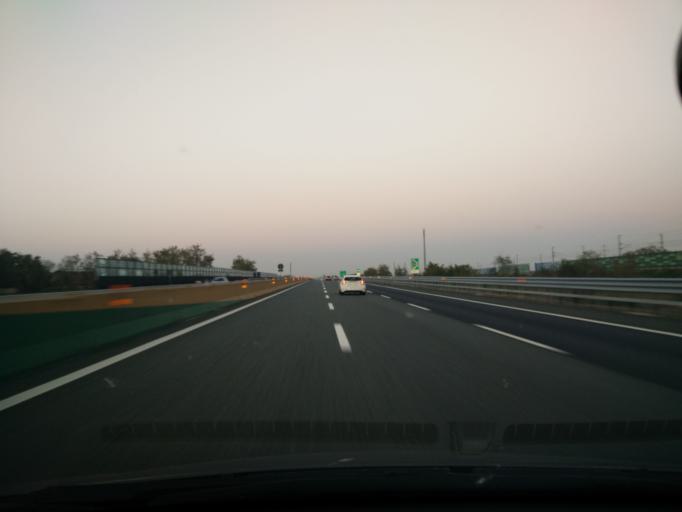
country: IT
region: Piedmont
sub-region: Provincia di Vercelli
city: Alice Castello
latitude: 45.3597
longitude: 8.1145
